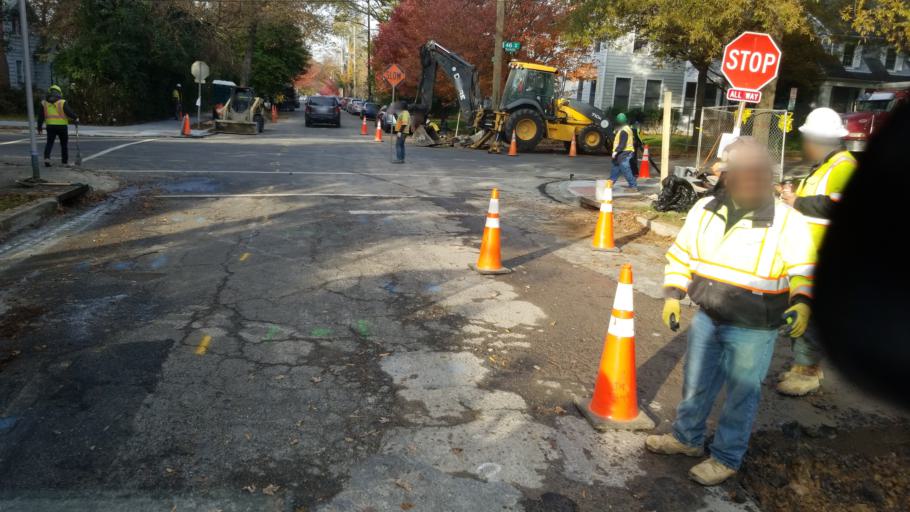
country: US
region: Maryland
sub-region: Montgomery County
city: Friendship Village
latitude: 38.9533
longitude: -77.0904
